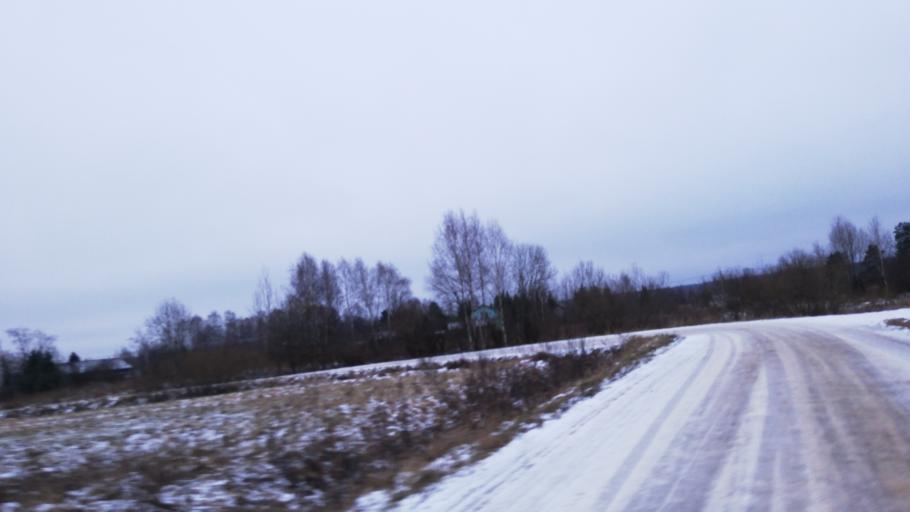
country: RU
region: Kostroma
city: Krasnoye-na-Volge
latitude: 57.6732
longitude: 41.1941
